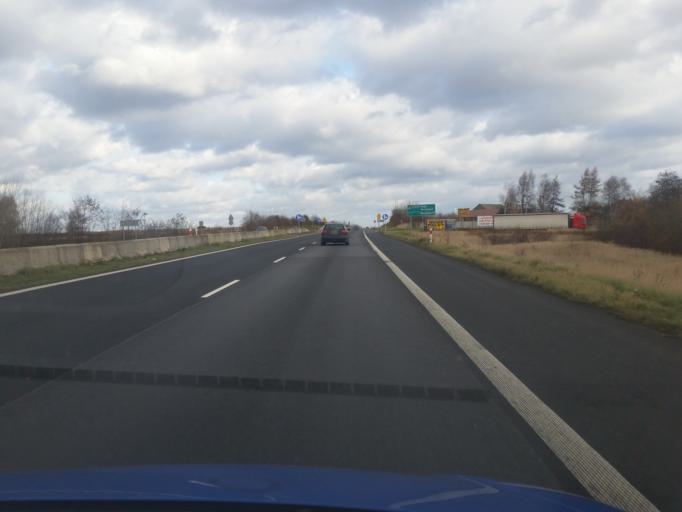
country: PL
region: Silesian Voivodeship
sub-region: Powiat czestochowski
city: Borowno
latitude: 50.9520
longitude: 19.2441
